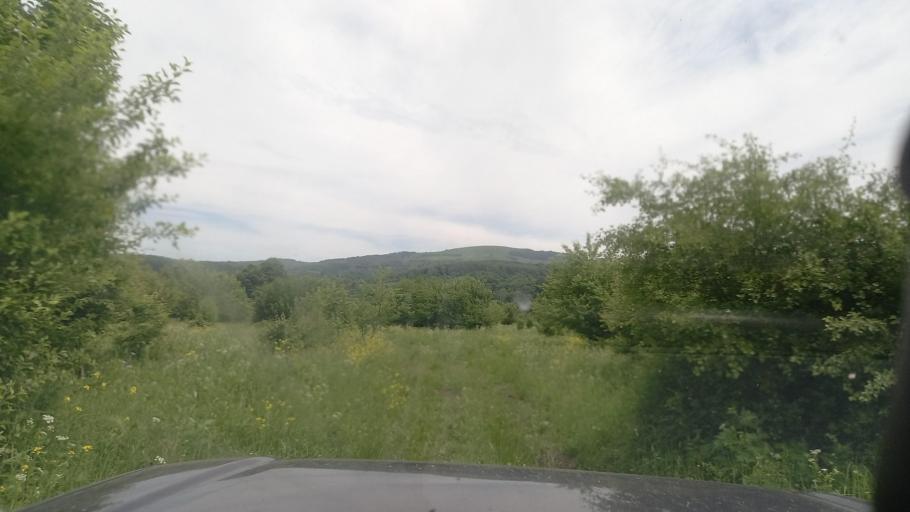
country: RU
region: Karachayevo-Cherkesiya
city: Pregradnaya
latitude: 44.1020
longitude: 41.1947
